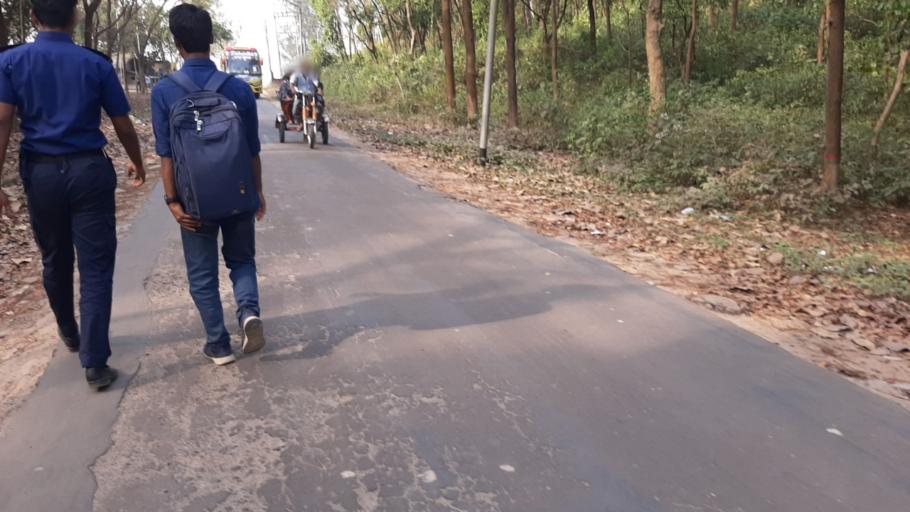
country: BD
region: Chittagong
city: Raojan
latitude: 22.4774
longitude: 91.7909
